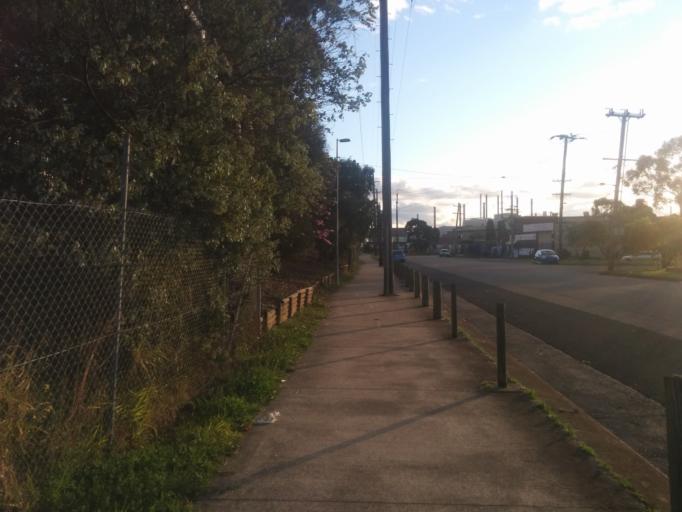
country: AU
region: New South Wales
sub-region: Fairfield
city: Fairfield East
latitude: -33.8640
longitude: 150.9716
